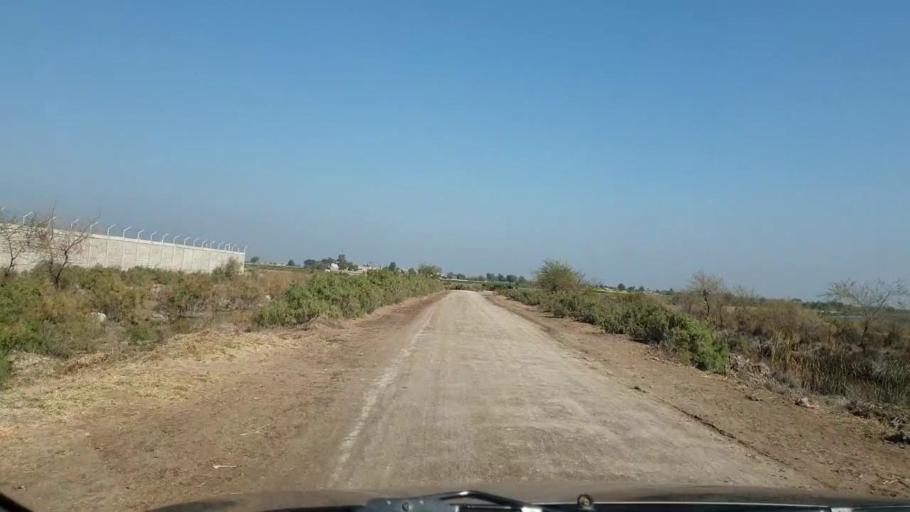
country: PK
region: Sindh
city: Sinjhoro
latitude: 25.9399
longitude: 68.7522
